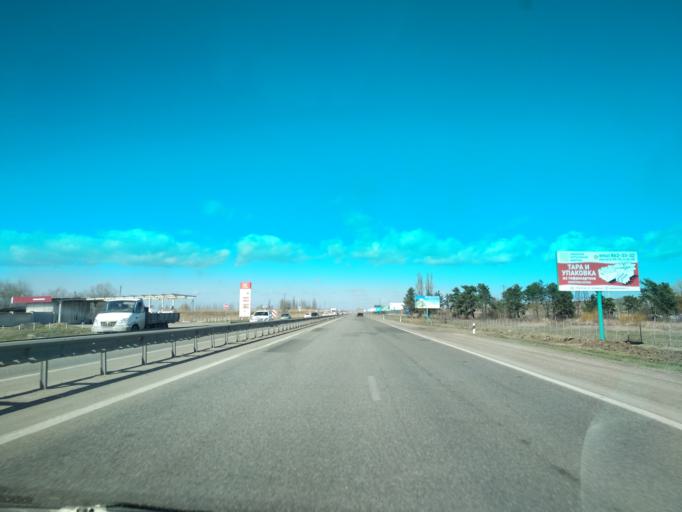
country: RU
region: Adygeya
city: Adygeysk
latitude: 44.9210
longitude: 39.1451
